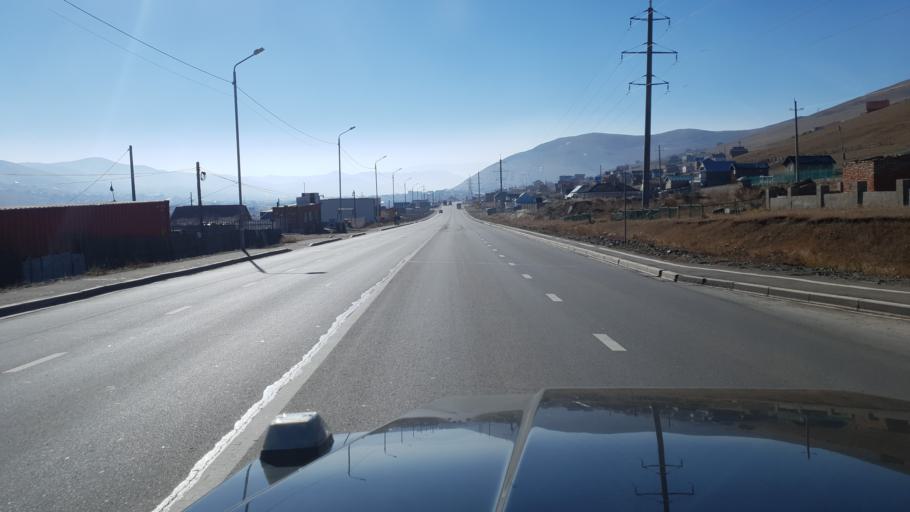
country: MN
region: Ulaanbaatar
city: Ulaanbaatar
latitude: 48.0290
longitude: 106.9115
